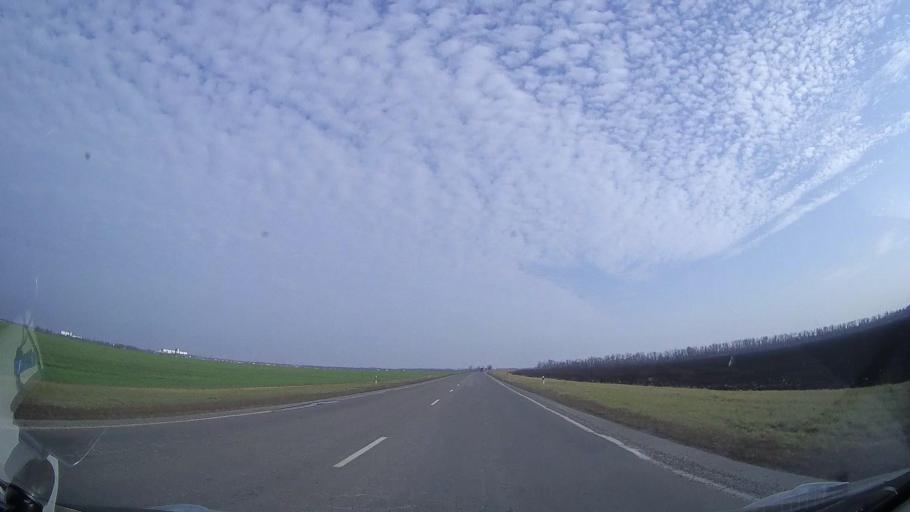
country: RU
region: Rostov
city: Tselina
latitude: 46.5126
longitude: 41.0278
